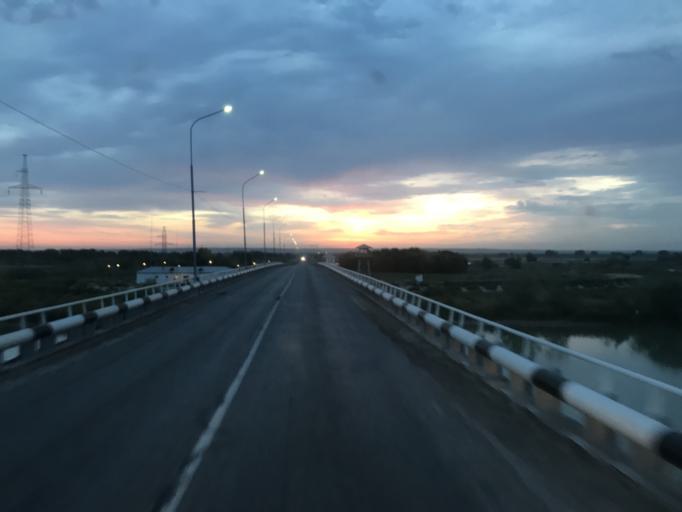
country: KZ
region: Ongtustik Qazaqstan
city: Ilyich
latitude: 41.0297
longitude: 68.5182
